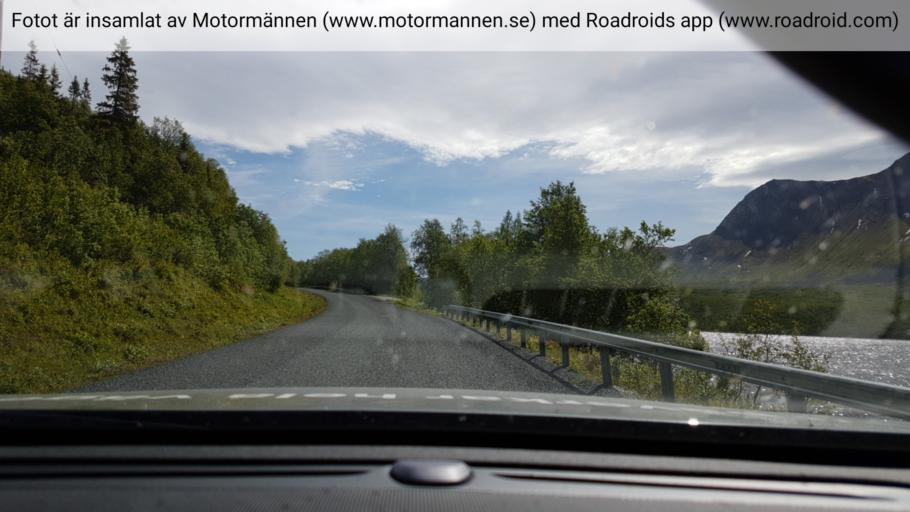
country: SE
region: Vaesterbotten
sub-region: Vilhelmina Kommun
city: Sjoberg
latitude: 65.2406
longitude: 15.4416
